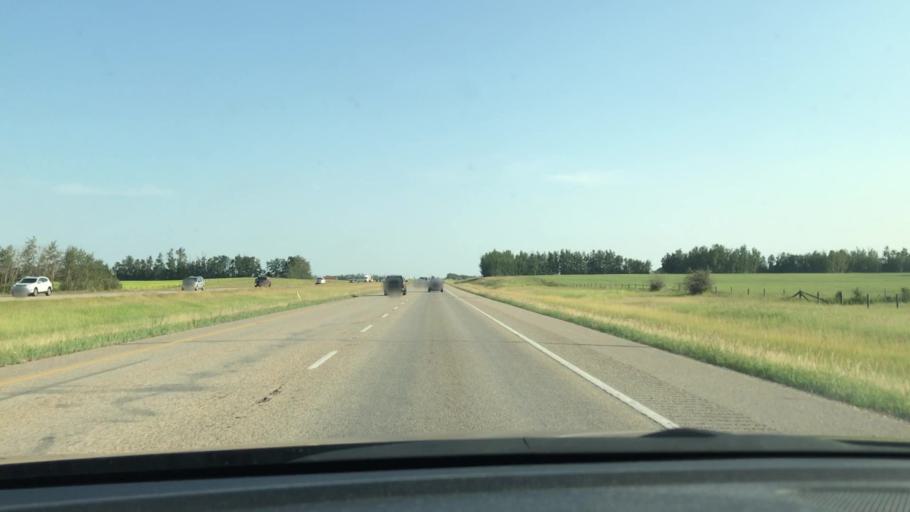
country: CA
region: Alberta
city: Millet
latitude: 53.1163
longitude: -113.5984
